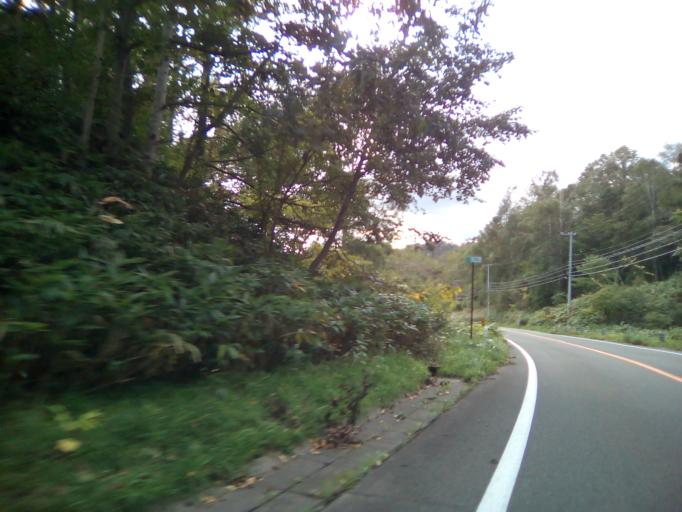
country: JP
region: Hokkaido
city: Date
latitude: 42.6623
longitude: 140.8294
